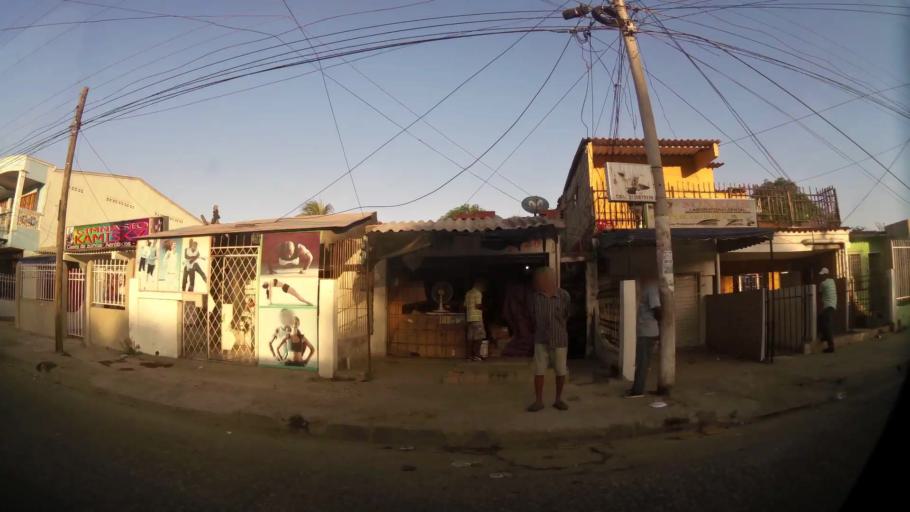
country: CO
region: Bolivar
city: Cartagena
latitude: 10.4344
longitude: -75.5292
